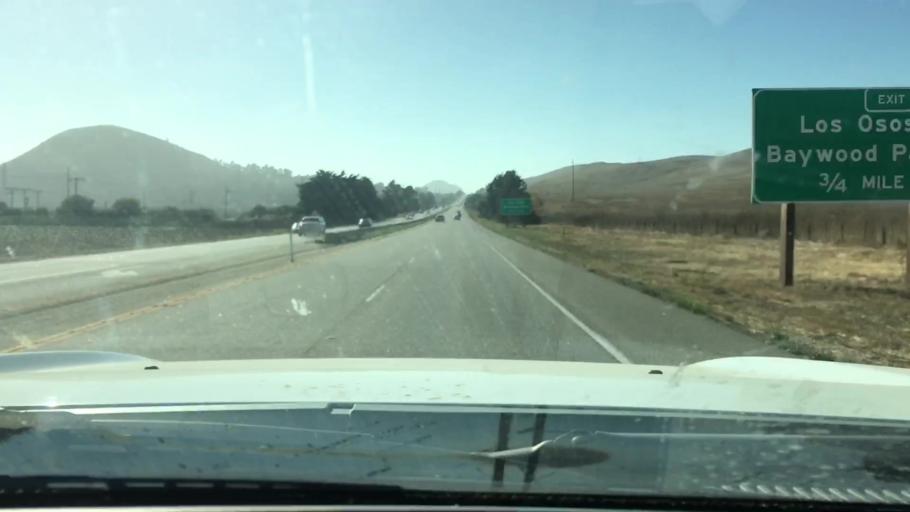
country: US
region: California
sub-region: San Luis Obispo County
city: Morro Bay
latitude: 35.3602
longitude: -120.8017
